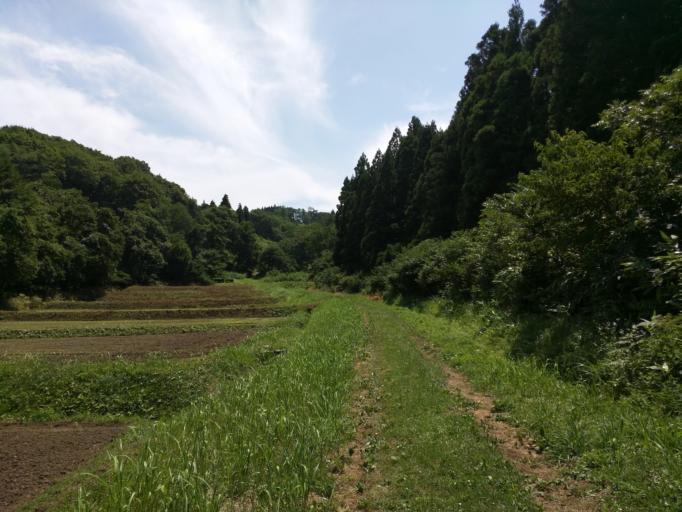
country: JP
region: Fukushima
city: Inawashiro
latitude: 37.5074
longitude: 139.9907
